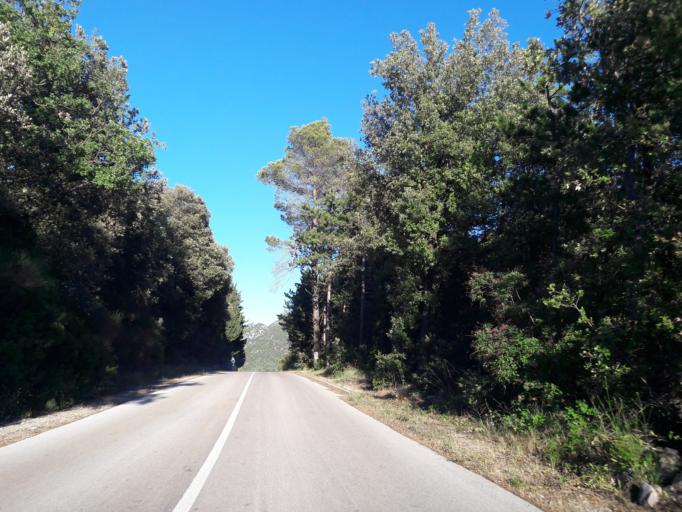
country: HR
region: Dubrovacko-Neretvanska
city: Orebic
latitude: 42.9989
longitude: 17.2582
